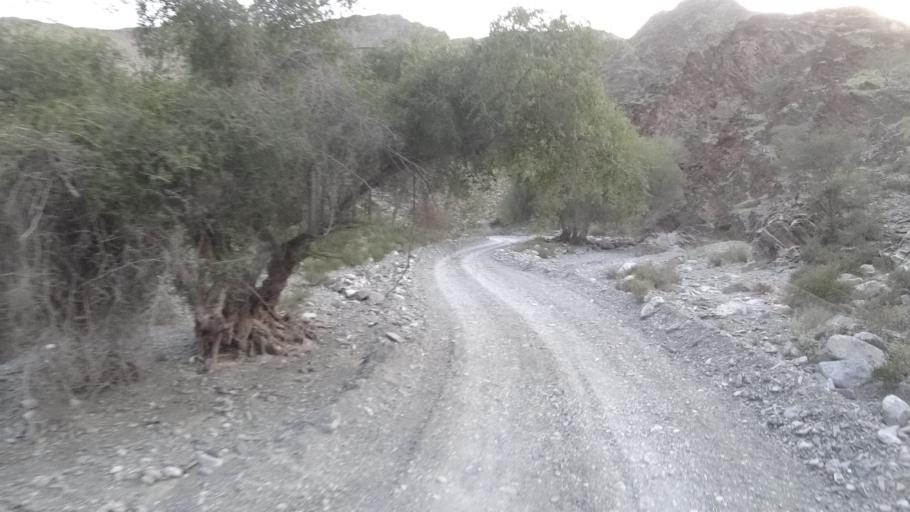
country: OM
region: Al Batinah
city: Bayt al `Awabi
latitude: 23.2362
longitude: 57.4459
